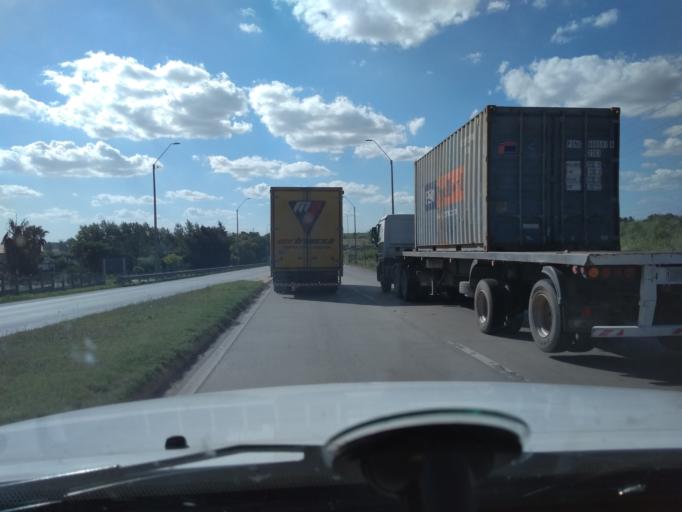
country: UY
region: Canelones
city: La Paz
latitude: -34.7839
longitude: -56.2250
